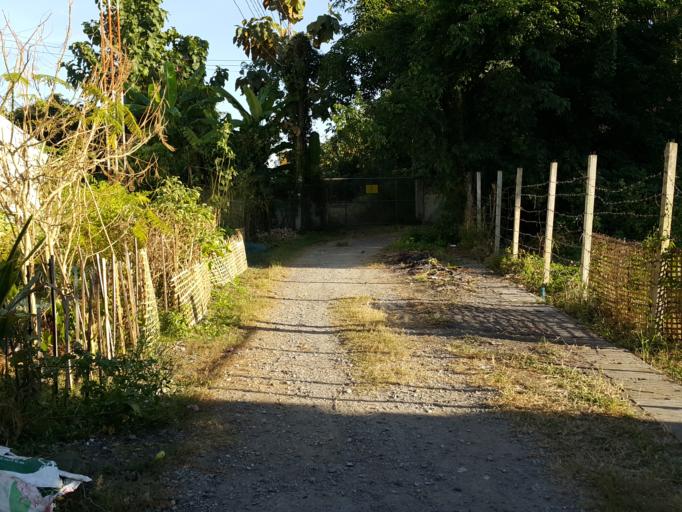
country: TH
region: Chiang Mai
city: San Kamphaeng
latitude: 18.7856
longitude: 99.1037
